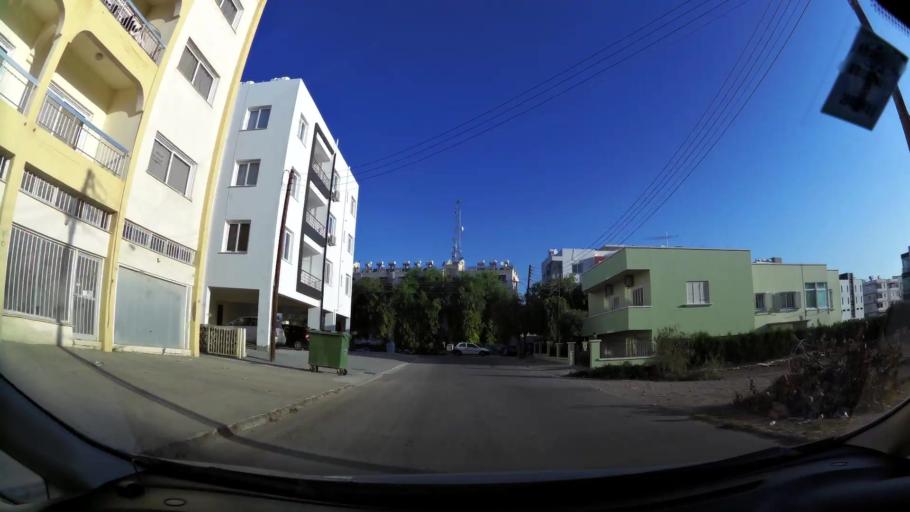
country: CY
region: Lefkosia
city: Nicosia
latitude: 35.2071
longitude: 33.3076
